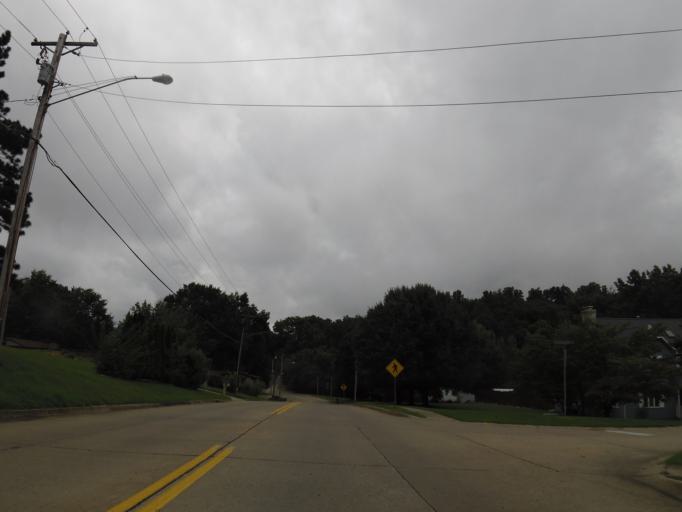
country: US
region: Missouri
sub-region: Cape Girardeau County
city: Cape Girardeau
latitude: 37.3518
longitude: -89.5604
